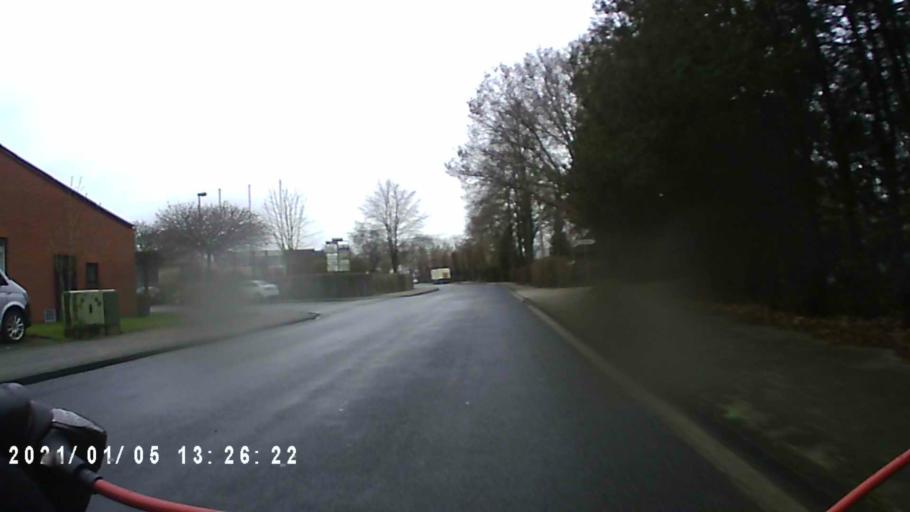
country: DE
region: Lower Saxony
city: Leer
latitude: 53.2292
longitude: 7.4336
